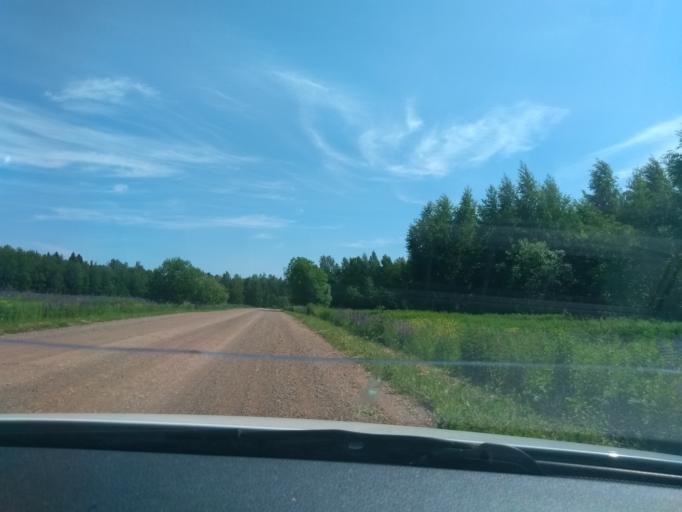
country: RU
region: Perm
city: Sylva
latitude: 57.8161
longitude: 56.7295
